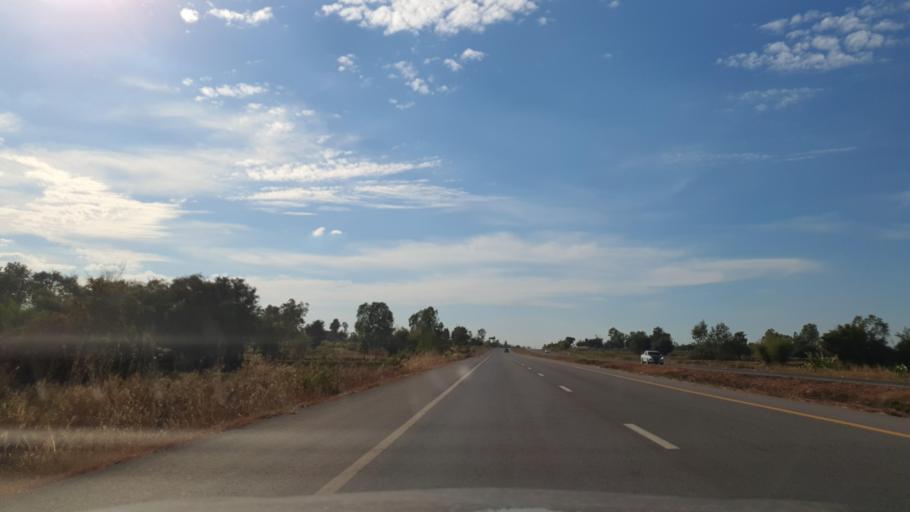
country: TH
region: Kalasin
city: Don Chan
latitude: 16.4112
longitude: 103.7501
